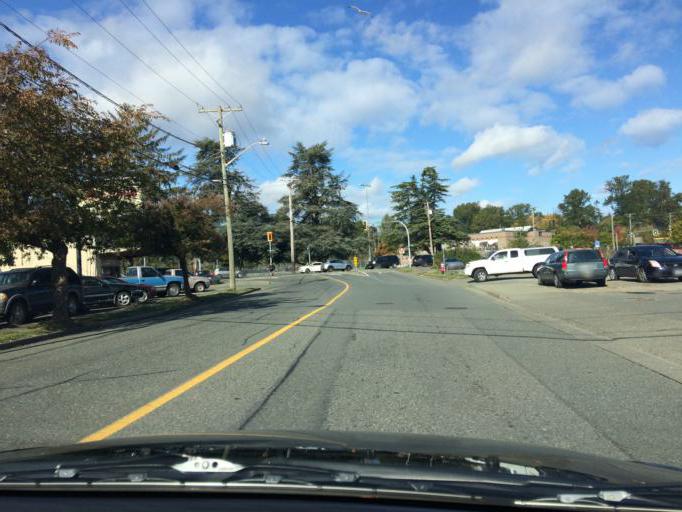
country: CA
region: British Columbia
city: Courtenay
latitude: 49.6932
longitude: -124.9920
